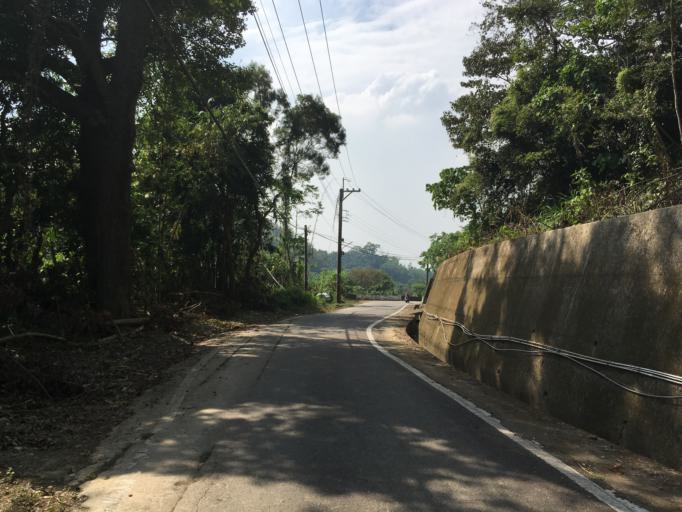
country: TW
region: Taiwan
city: Fengyuan
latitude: 24.1843
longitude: 120.7839
